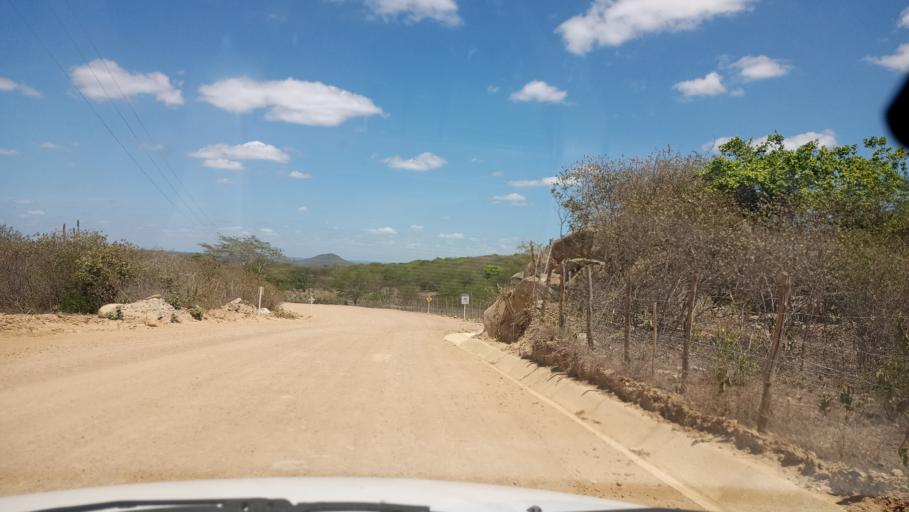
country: BR
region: Rio Grande do Norte
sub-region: Sao Paulo Do Potengi
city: Sao Paulo do Potengi
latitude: -5.7725
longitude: -35.9121
